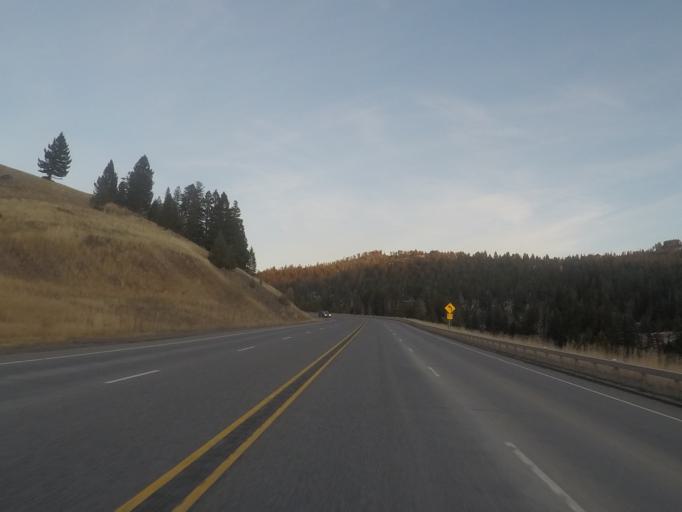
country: US
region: Montana
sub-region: Lewis and Clark County
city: Helena West Side
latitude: 46.5569
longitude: -112.3666
